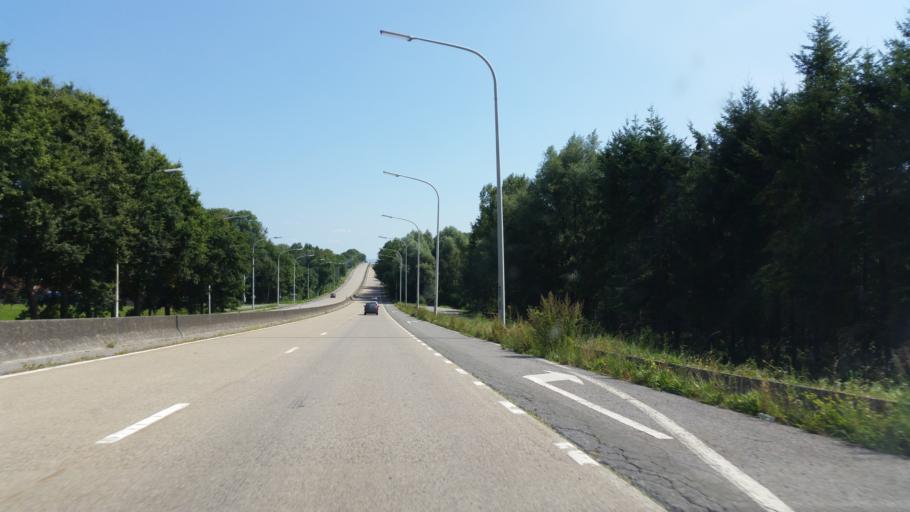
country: BE
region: Wallonia
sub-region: Province de Namur
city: Hamois
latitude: 50.2804
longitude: 5.2016
